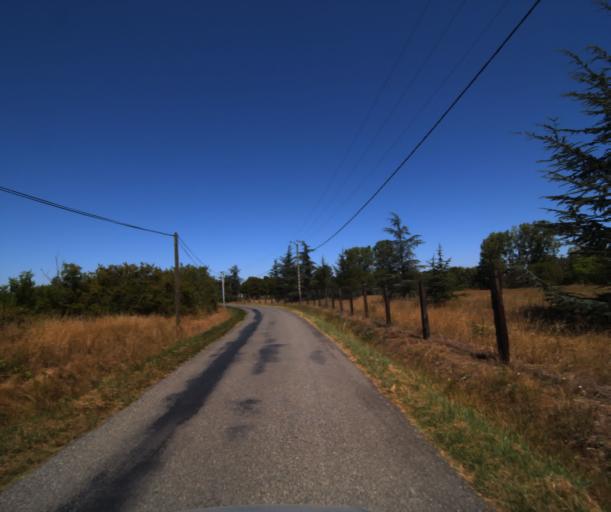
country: FR
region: Midi-Pyrenees
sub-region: Departement de la Haute-Garonne
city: Seysses
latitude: 43.4761
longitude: 1.2940
